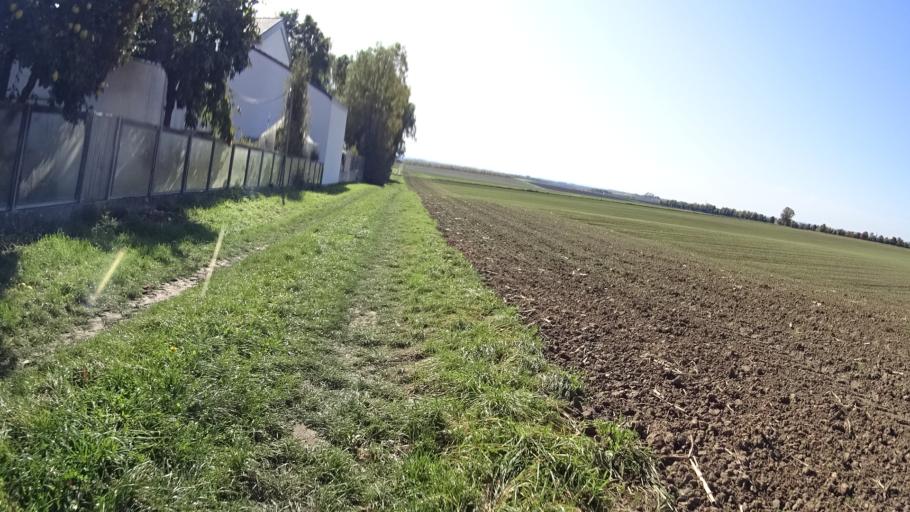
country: DE
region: Bavaria
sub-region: Upper Bavaria
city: Gaimersheim
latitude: 48.8352
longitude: 11.3509
